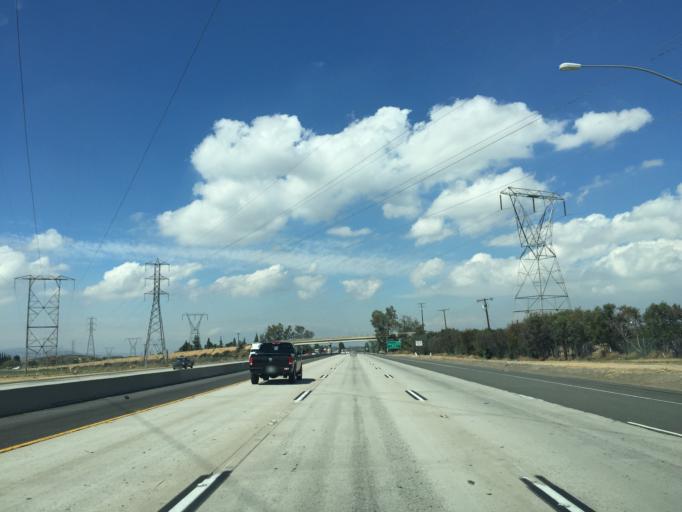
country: US
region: California
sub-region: Riverside County
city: Cherry Valley
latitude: 33.9592
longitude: -117.0220
